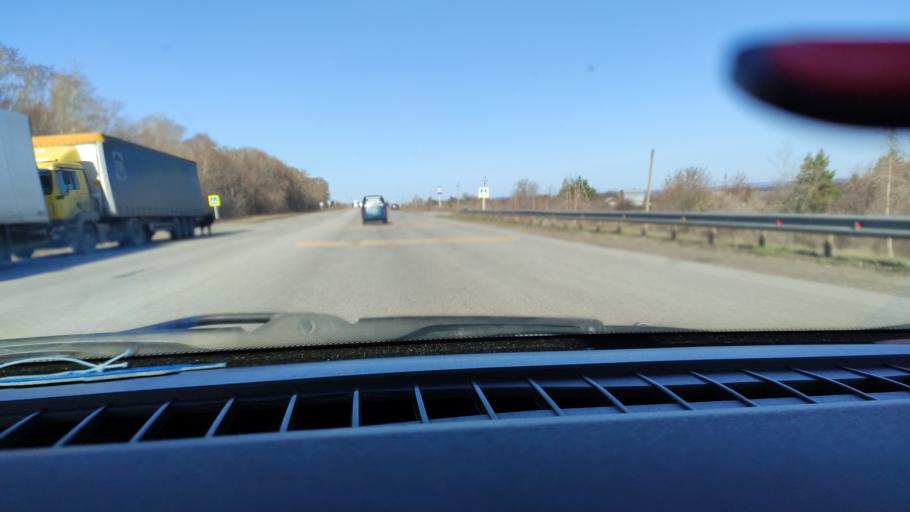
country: RU
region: Samara
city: Varlamovo
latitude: 53.1226
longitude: 48.3074
